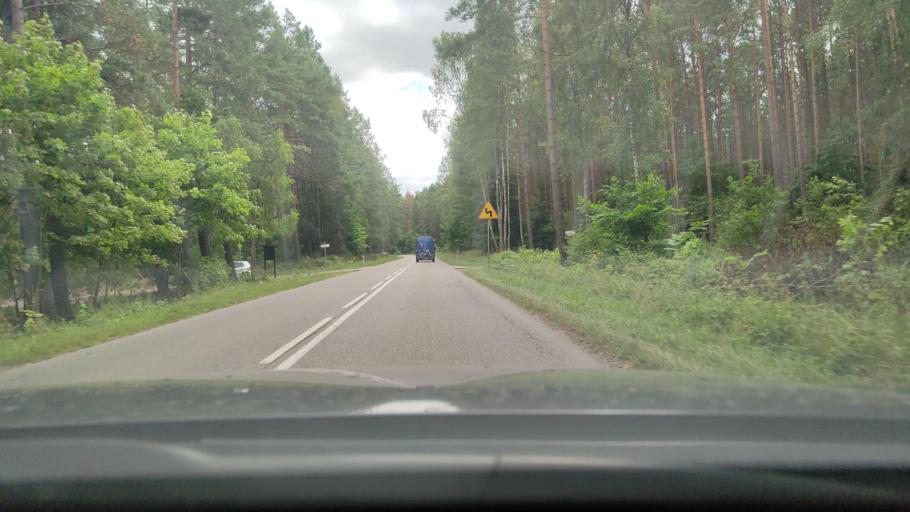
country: PL
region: Pomeranian Voivodeship
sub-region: Powiat wejherowski
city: Orle
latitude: 54.6491
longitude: 18.2126
